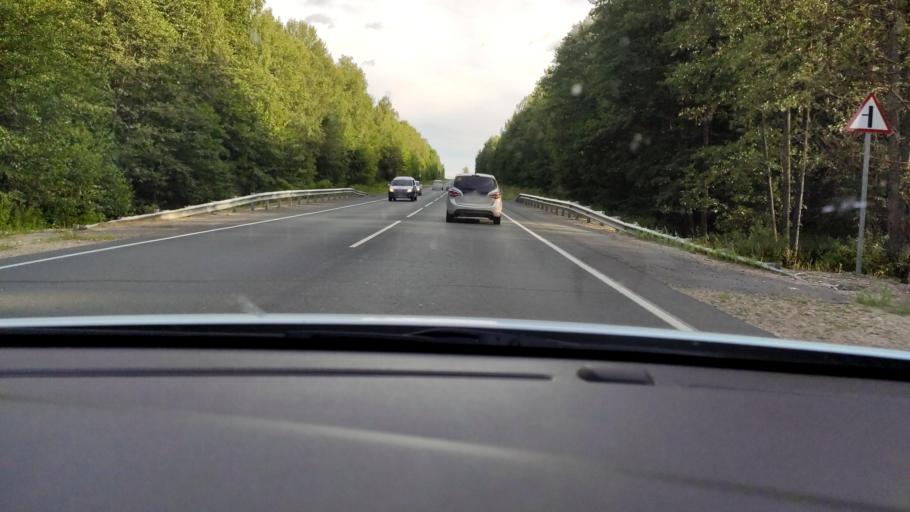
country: RU
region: Mariy-El
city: Suslonger
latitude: 56.2318
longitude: 48.2329
